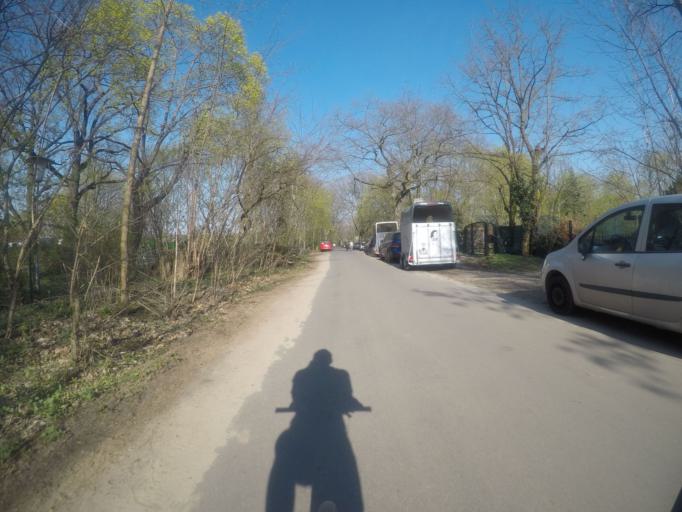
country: DE
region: Berlin
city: Zehlendorf Bezirk
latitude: 52.4290
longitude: 13.2387
